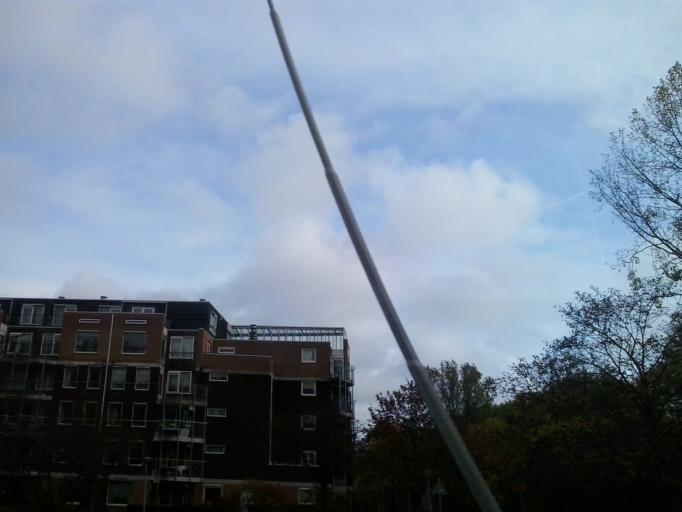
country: NL
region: South Holland
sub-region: Gemeente Delft
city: Delft
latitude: 52.0093
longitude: 4.3414
